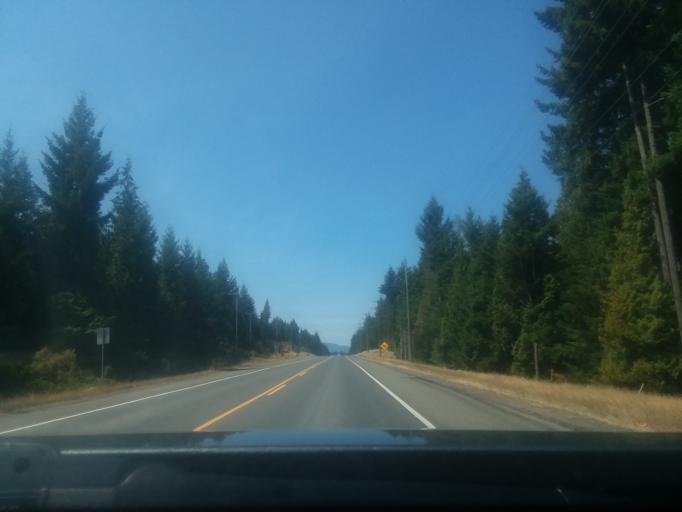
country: CA
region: British Columbia
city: Courtenay
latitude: 49.7152
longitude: -124.9384
